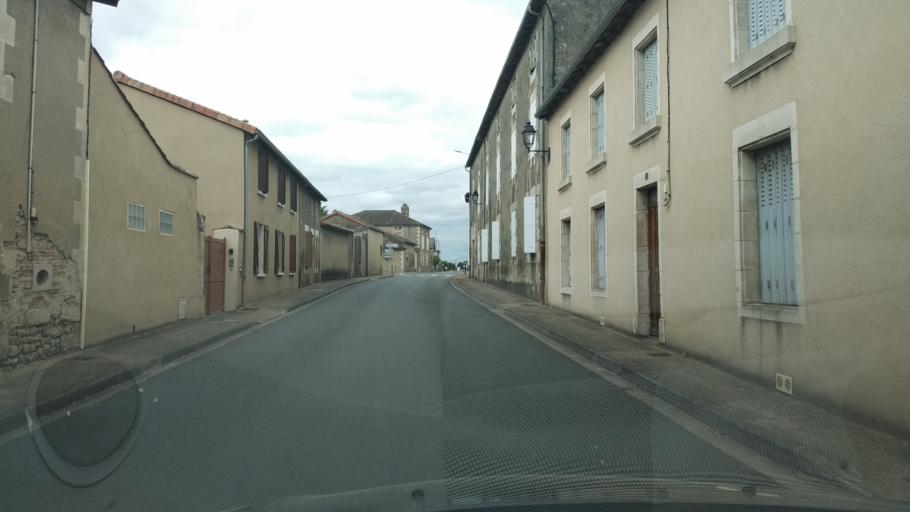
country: FR
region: Poitou-Charentes
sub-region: Departement de la Vienne
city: La Villedieu-du-Clain
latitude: 46.4572
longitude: 0.3671
